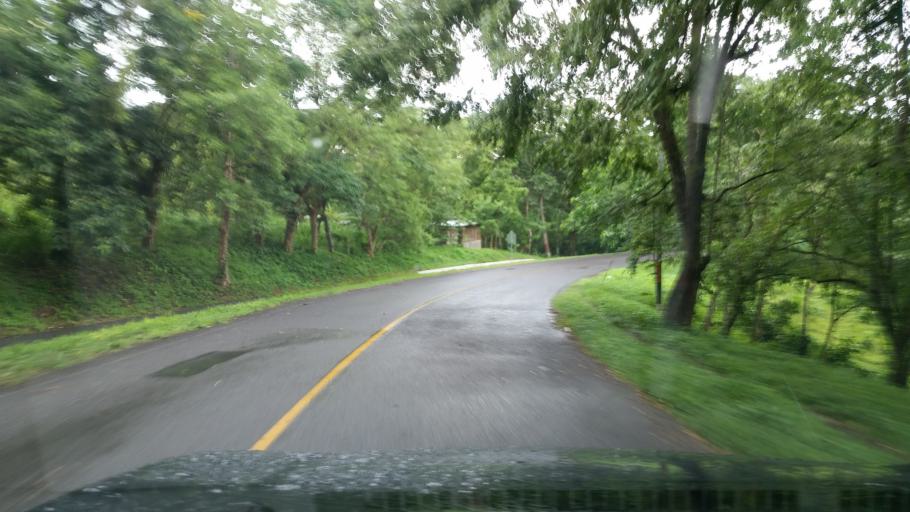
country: NI
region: Matagalpa
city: San Ramon
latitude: 13.0421
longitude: -85.7699
